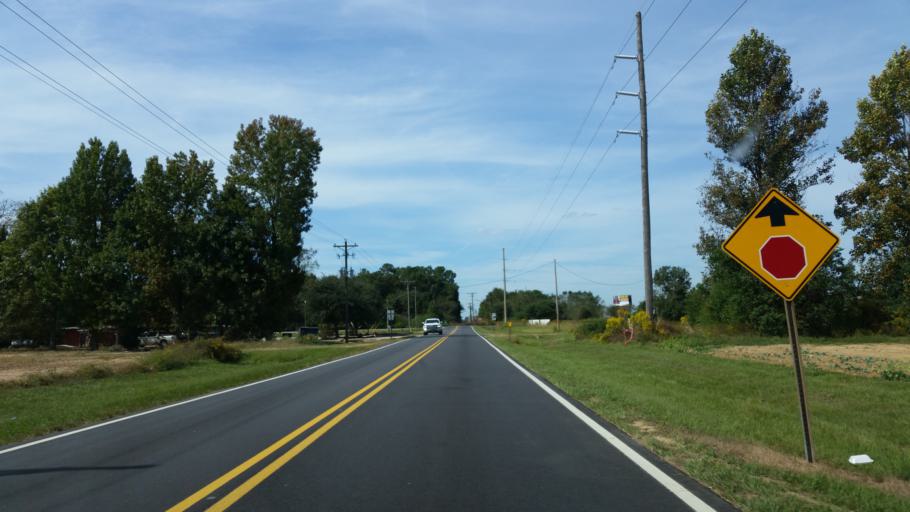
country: US
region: Alabama
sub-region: Baldwin County
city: Loxley
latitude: 30.6330
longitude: -87.7540
